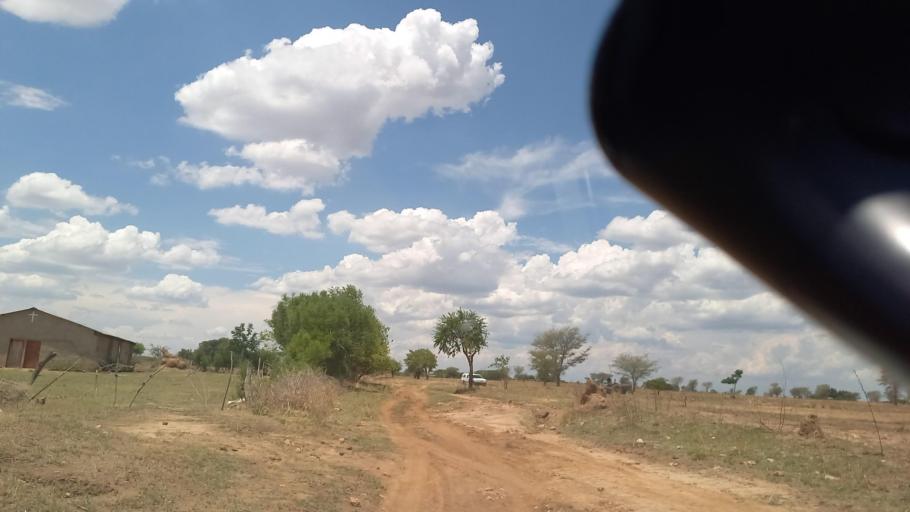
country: ZM
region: Southern
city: Mazabuka
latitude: -16.1148
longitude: 27.8138
